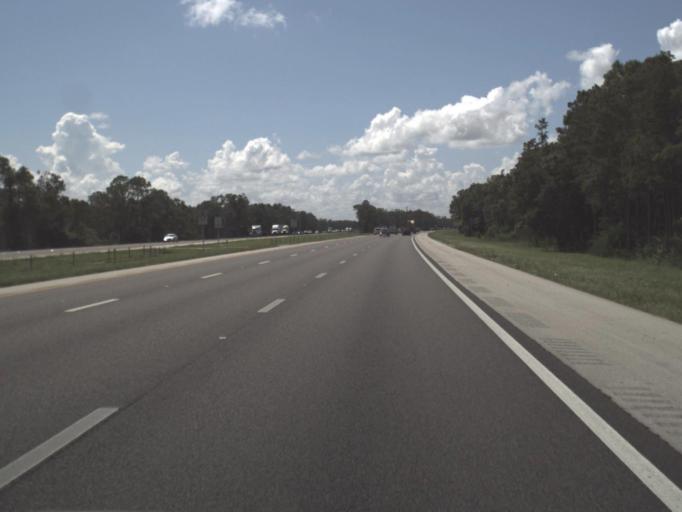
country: US
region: Florida
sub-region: Lee County
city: Gateway
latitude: 26.5865
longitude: -81.7957
